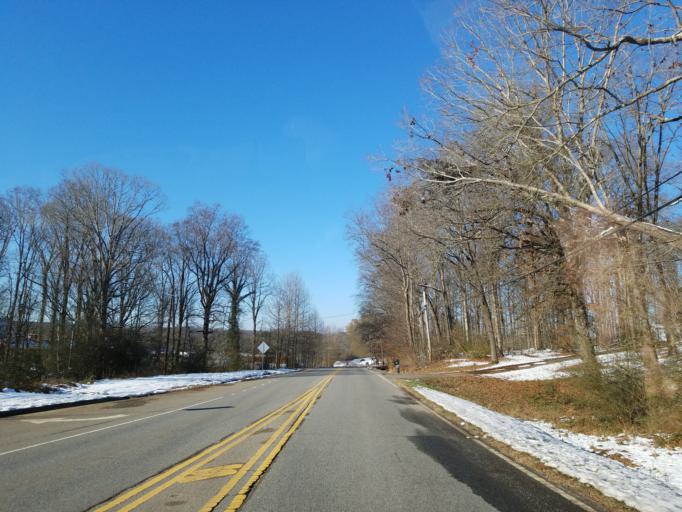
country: US
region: Georgia
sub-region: Forsyth County
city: Cumming
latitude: 34.3009
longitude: -84.1001
